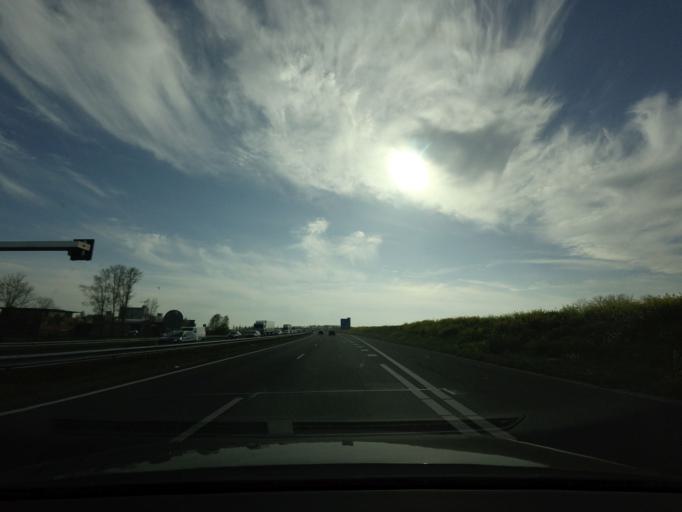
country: NL
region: North Brabant
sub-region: Gemeente Veghel
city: Eerde
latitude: 51.6297
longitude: 5.5108
